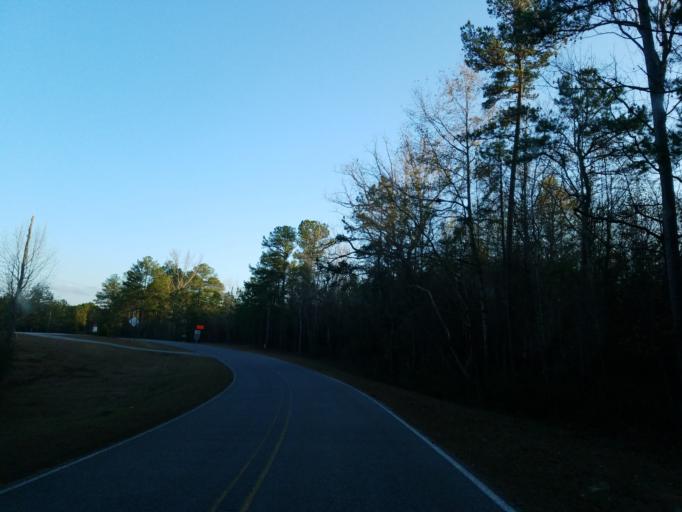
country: US
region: Mississippi
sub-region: Clarke County
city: Stonewall
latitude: 32.2647
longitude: -88.8118
